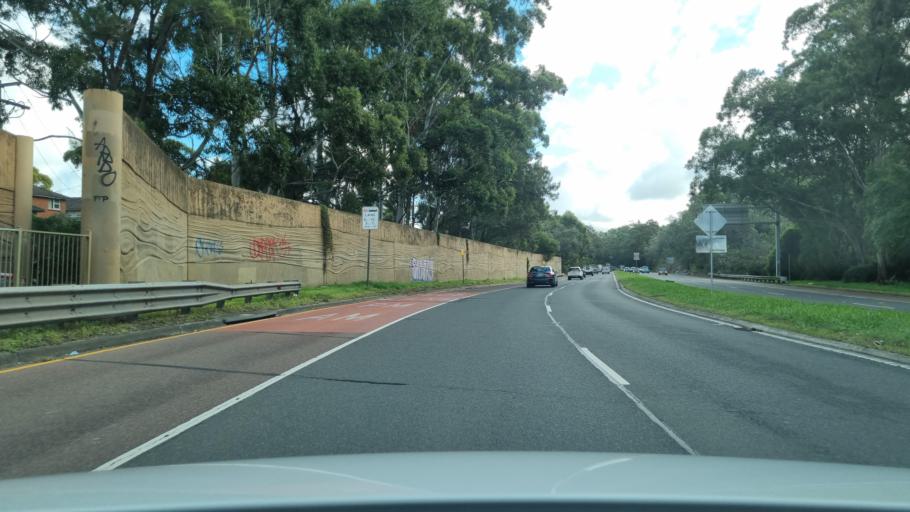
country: AU
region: New South Wales
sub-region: Manly Vale
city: Balgowlah
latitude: -33.7889
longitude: 151.2647
